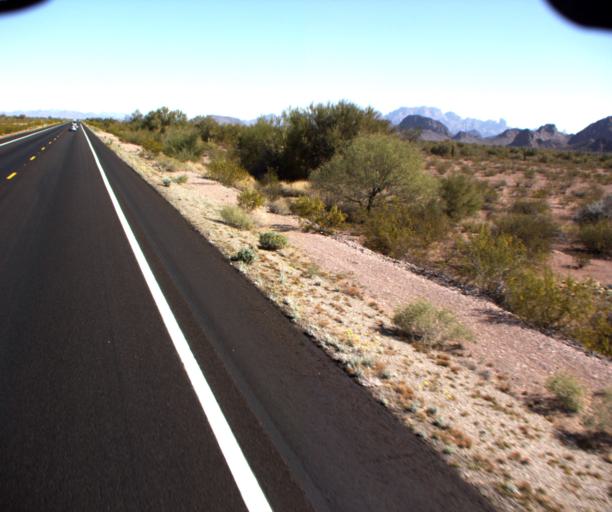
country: US
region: Arizona
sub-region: La Paz County
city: Quartzsite
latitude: 33.2762
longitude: -114.2339
